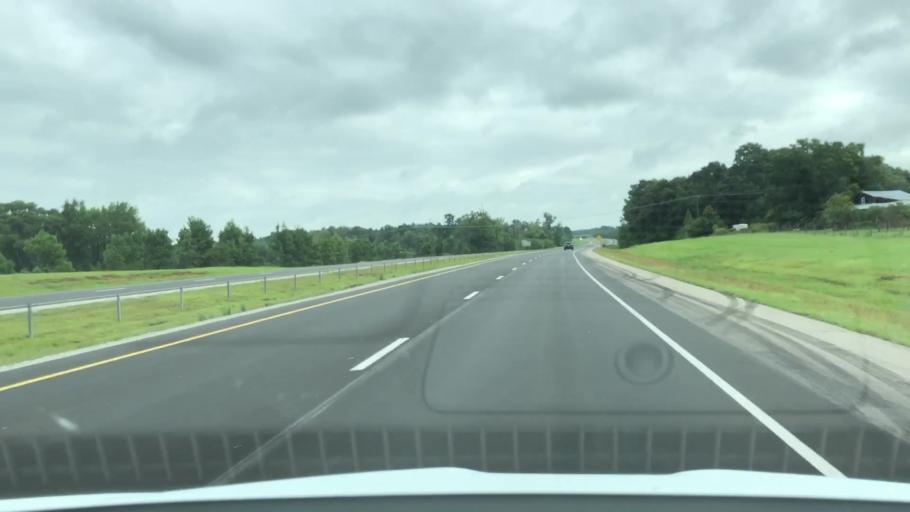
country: US
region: North Carolina
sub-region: Wilson County
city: Lucama
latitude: 35.6335
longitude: -77.9713
